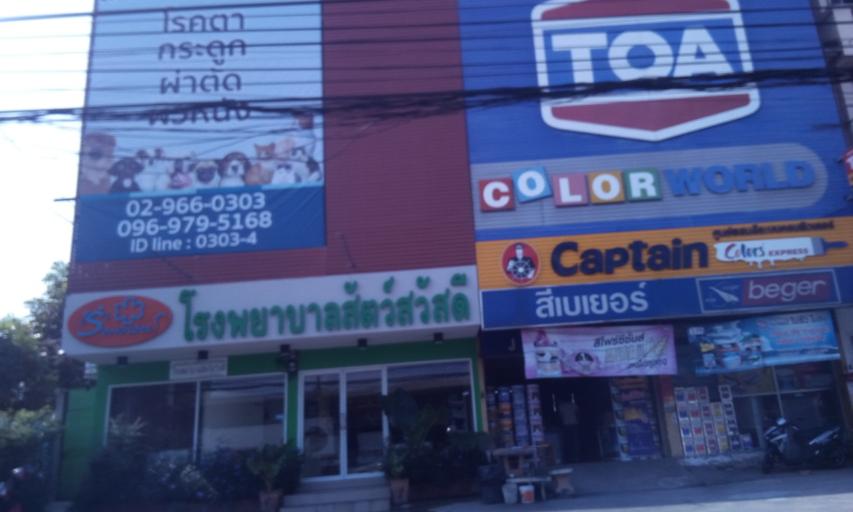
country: TH
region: Bangkok
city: Sai Mai
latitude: 13.9321
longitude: 100.6695
